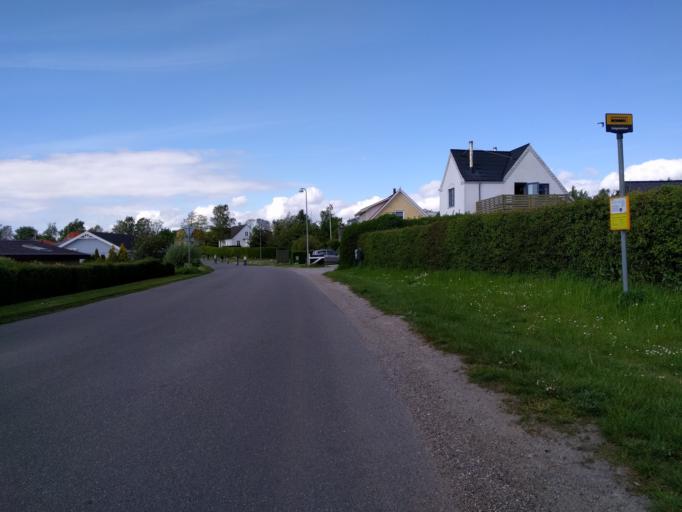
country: DK
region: Zealand
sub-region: Guldborgsund Kommune
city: Stubbekobing
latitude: 54.9150
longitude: 12.0509
